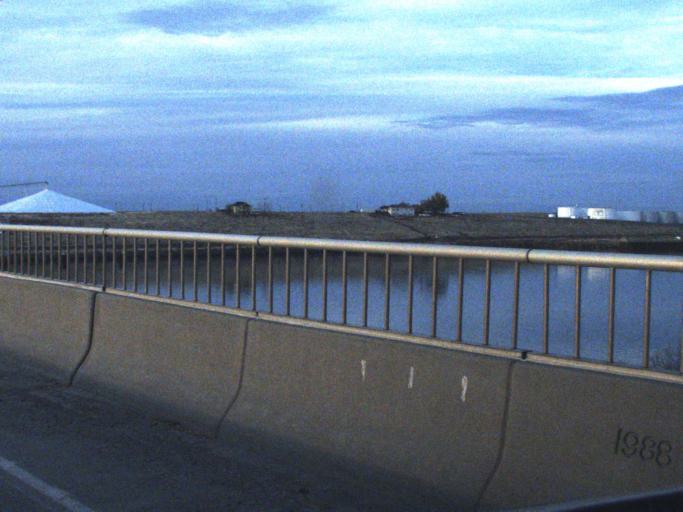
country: US
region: Washington
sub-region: Walla Walla County
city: Burbank
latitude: 46.2143
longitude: -119.0201
